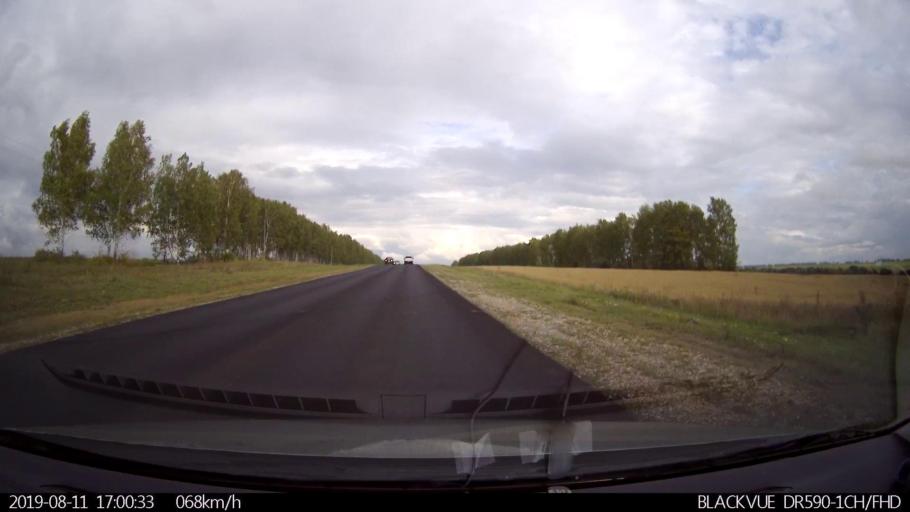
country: RU
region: Ulyanovsk
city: Mayna
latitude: 54.3101
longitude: 47.6814
